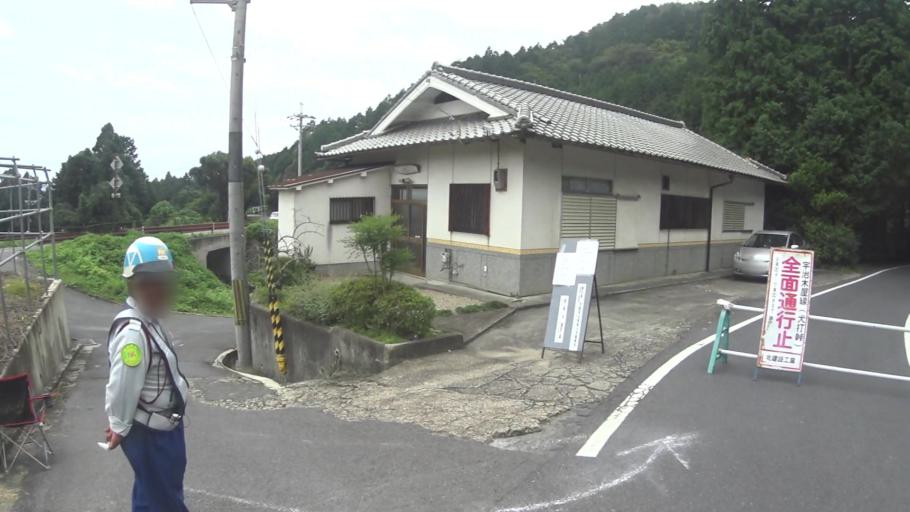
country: JP
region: Kyoto
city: Uji
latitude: 34.8076
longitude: 135.8965
